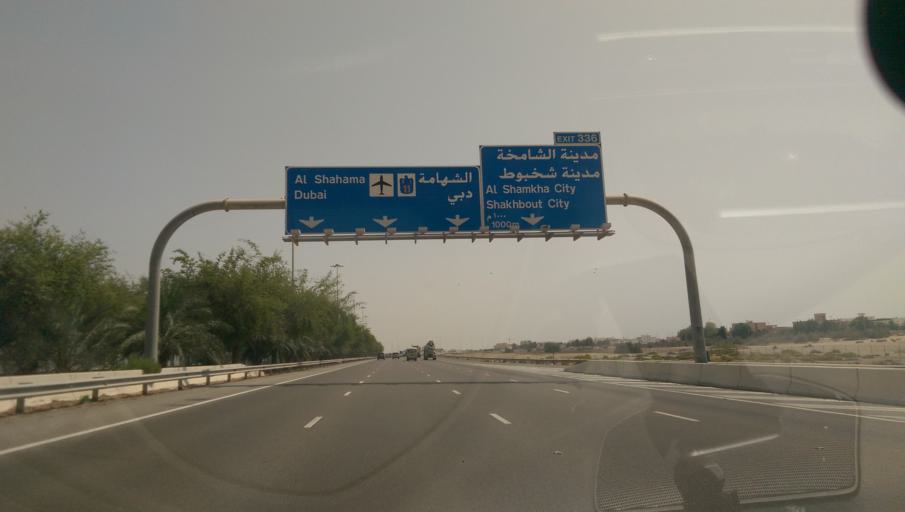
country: AE
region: Abu Dhabi
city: Abu Dhabi
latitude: 24.3574
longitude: 54.6481
